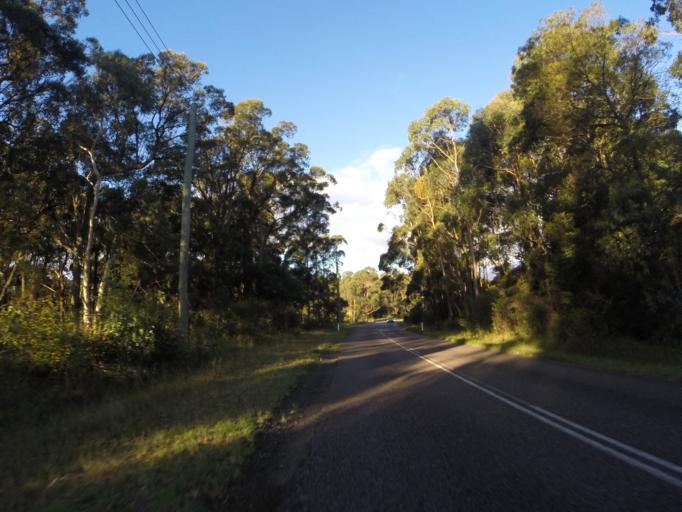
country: AU
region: New South Wales
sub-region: Shoalhaven Shire
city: Kangaroo Valley
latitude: -34.6469
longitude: 150.5072
